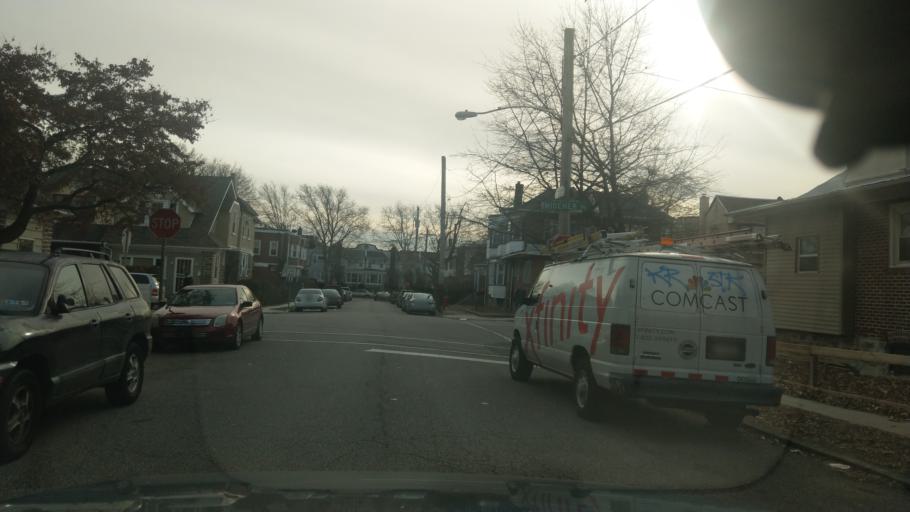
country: US
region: Pennsylvania
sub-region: Montgomery County
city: Wyncote
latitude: 40.0442
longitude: -75.1453
